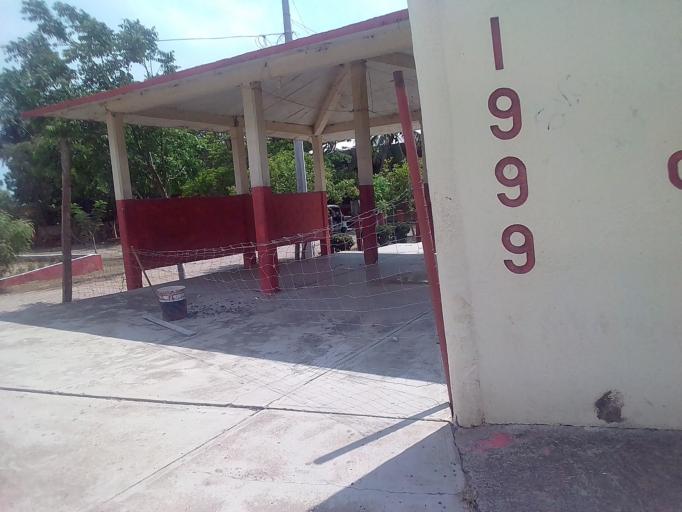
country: MX
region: Oaxaca
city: Union Hidalgo
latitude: 16.4562
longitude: -94.8291
